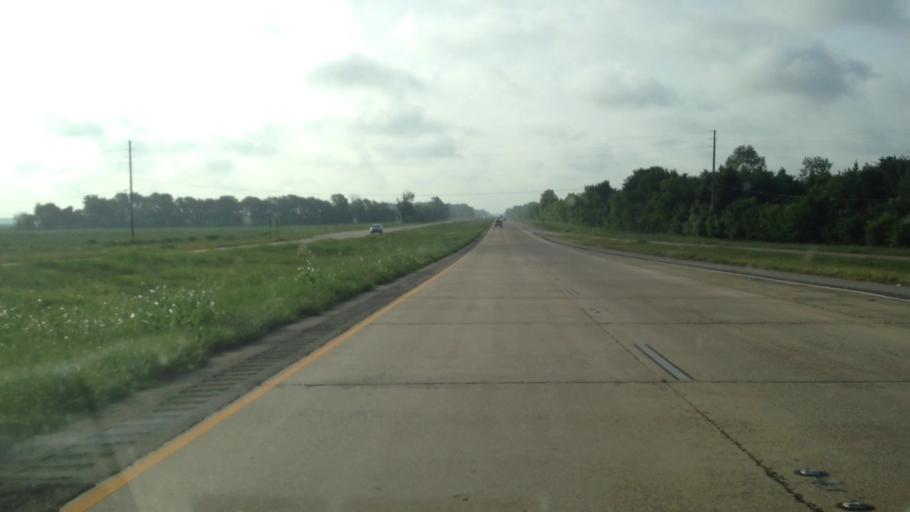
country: US
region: Louisiana
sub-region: Rapides Parish
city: Lecompte
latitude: 31.0133
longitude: -92.3733
